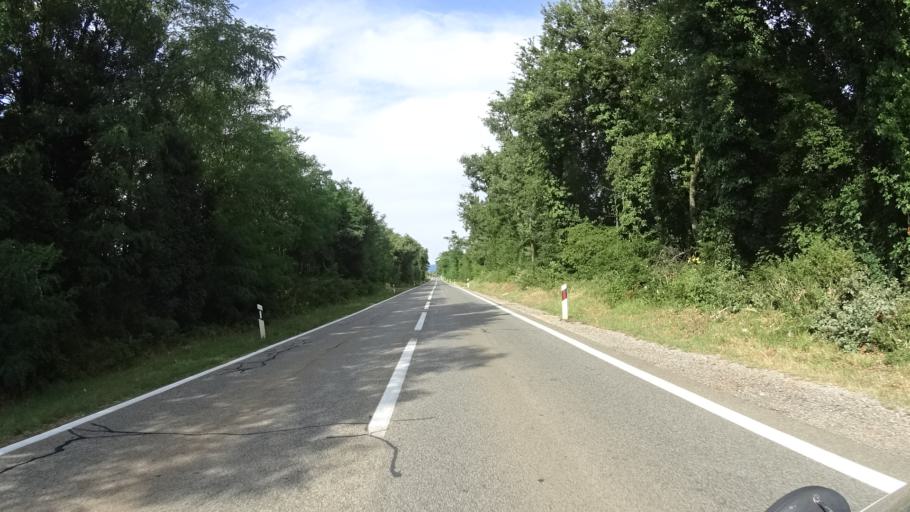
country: HR
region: Istarska
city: Marcana
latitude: 44.9433
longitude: 13.9399
